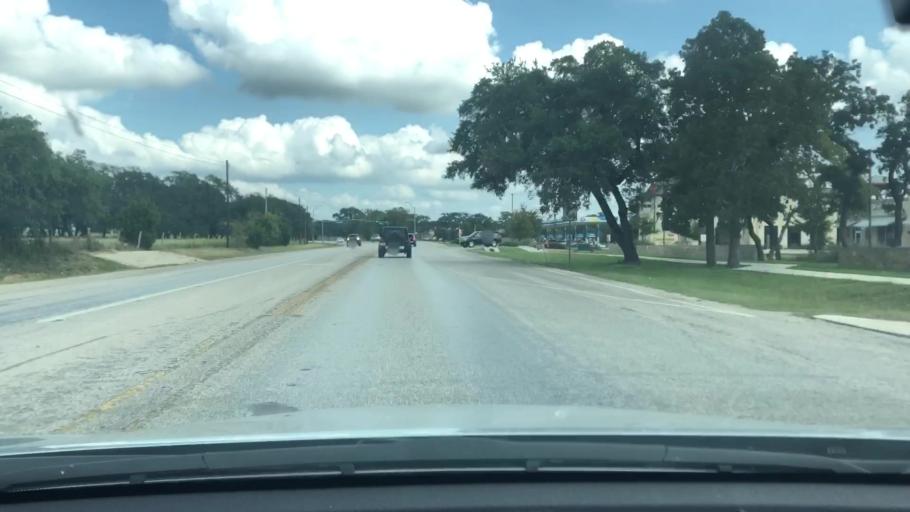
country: US
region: Texas
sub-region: Kendall County
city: Boerne
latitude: 29.7878
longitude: -98.6999
